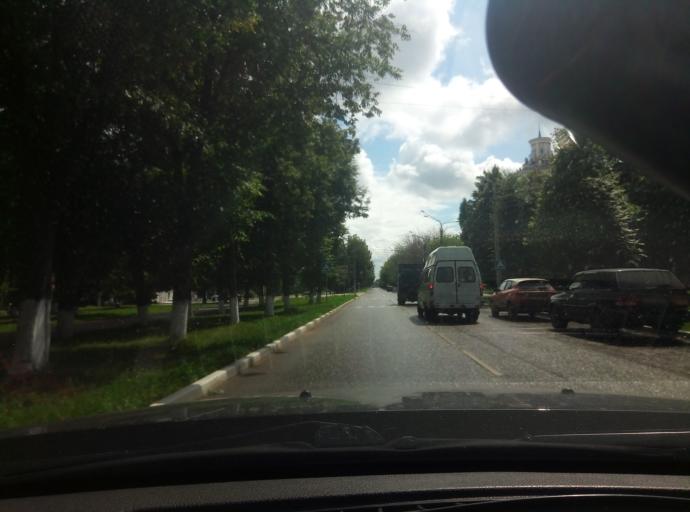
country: RU
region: Tula
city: Novomoskovsk
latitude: 54.0118
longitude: 38.2961
